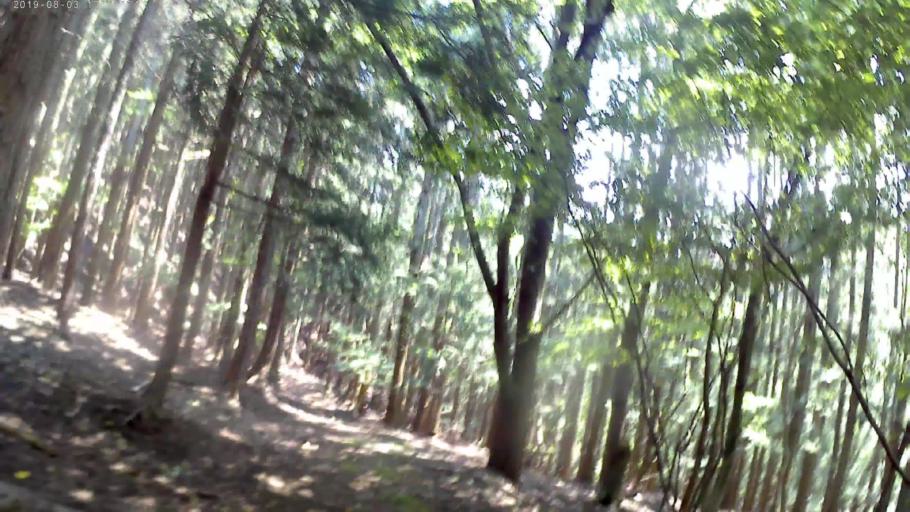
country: JP
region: Yamanashi
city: Enzan
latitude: 35.6089
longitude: 138.7905
